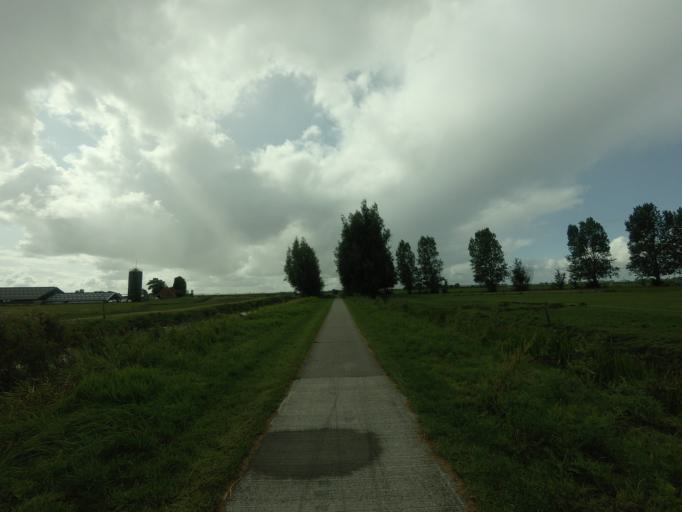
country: NL
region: Friesland
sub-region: Gemeente Boarnsterhim
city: Wergea
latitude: 53.1465
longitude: 5.8253
